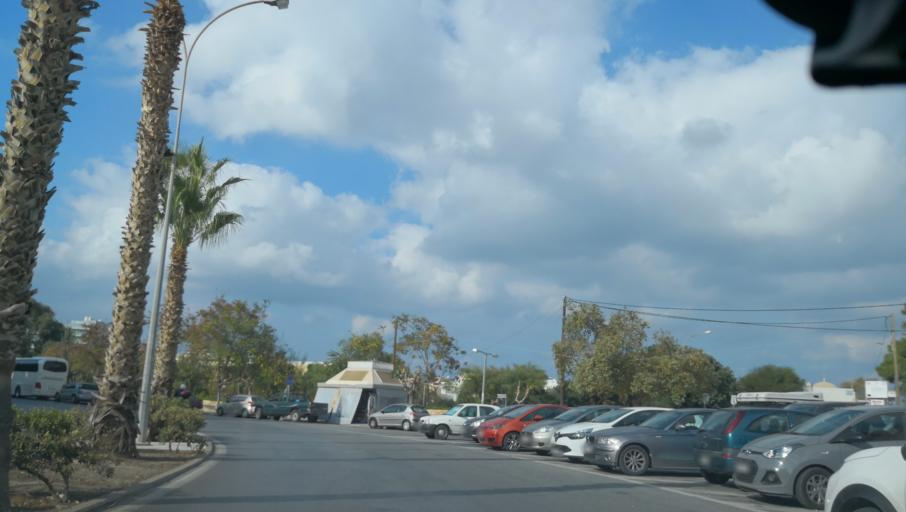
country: GR
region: Crete
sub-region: Nomos Irakleiou
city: Irakleion
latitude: 35.3363
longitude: 25.1389
